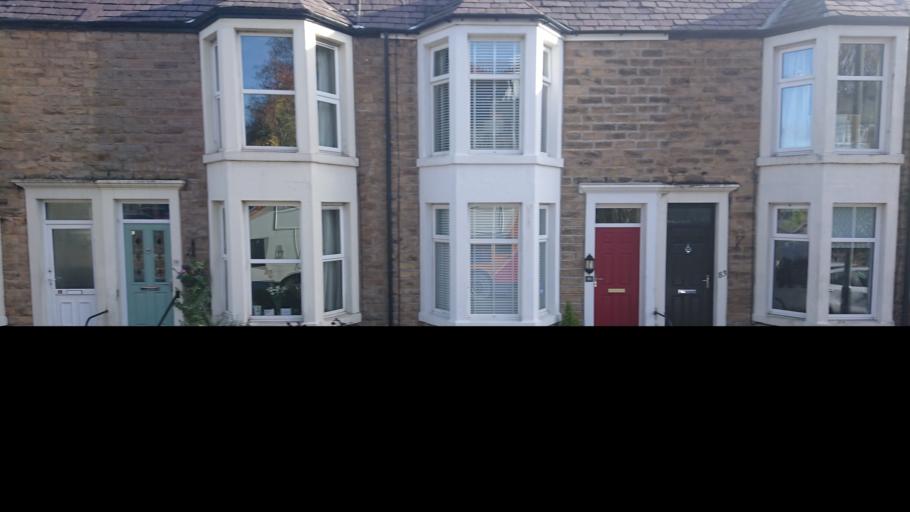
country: GB
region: England
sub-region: Lancashire
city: Lancaster
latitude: 54.0316
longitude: -2.7944
